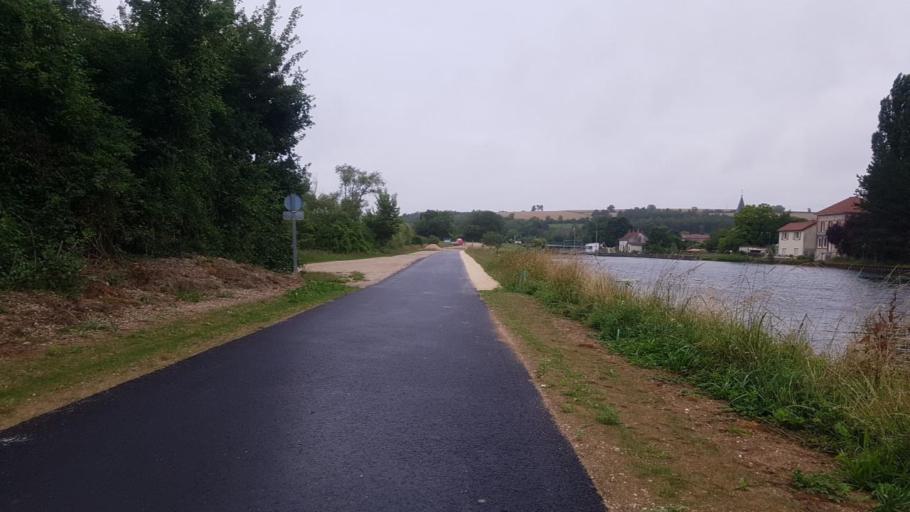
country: FR
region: Champagne-Ardenne
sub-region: Departement de la Marne
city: Vitry-le-Francois
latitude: 48.7887
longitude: 4.5340
